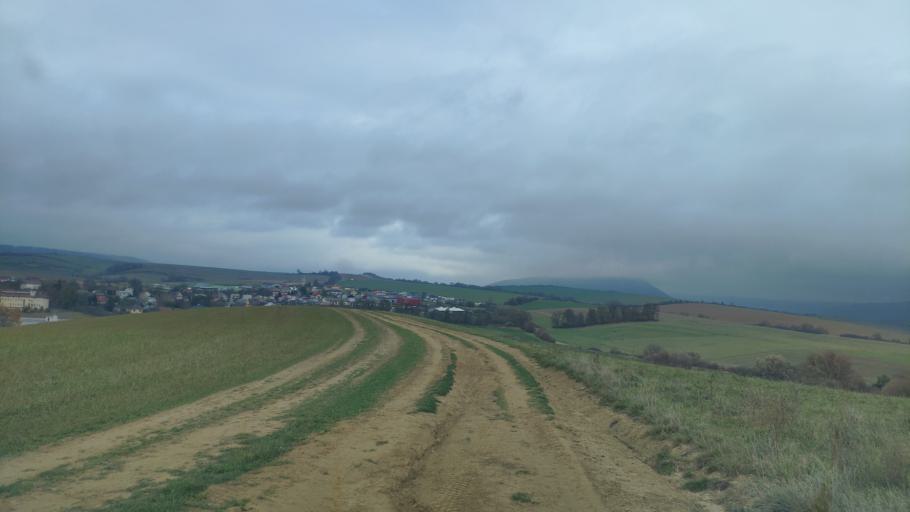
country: SK
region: Presovsky
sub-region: Okres Presov
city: Presov
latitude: 49.0089
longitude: 21.1942
